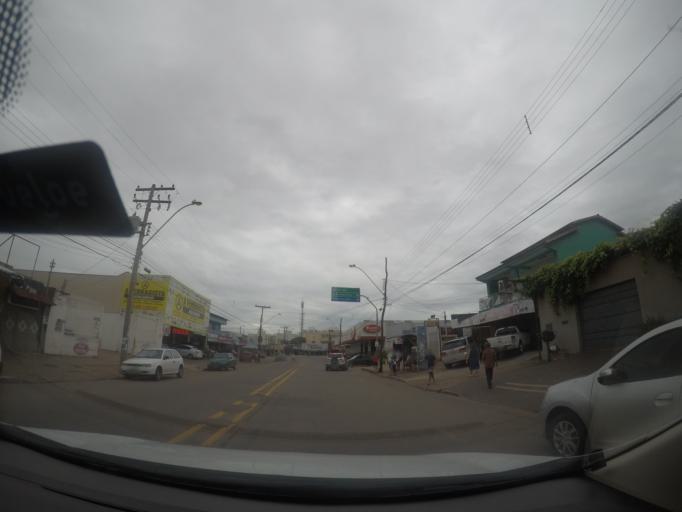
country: BR
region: Goias
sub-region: Goiania
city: Goiania
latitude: -16.6223
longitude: -49.2850
